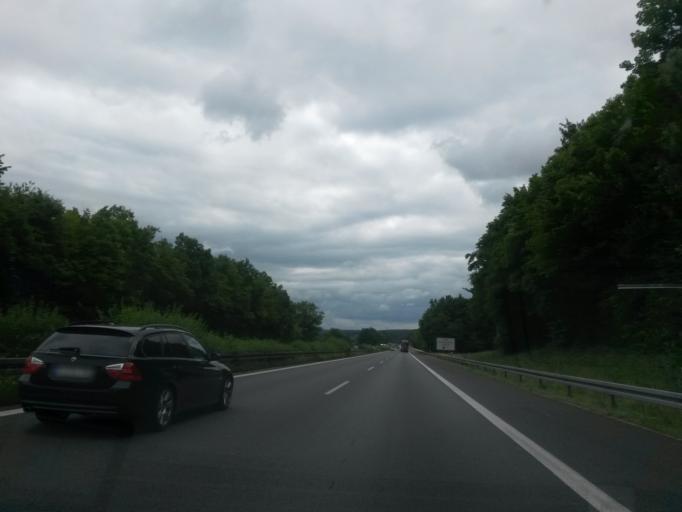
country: DE
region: Bavaria
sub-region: Upper Franconia
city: Schlusselfeld
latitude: 49.7547
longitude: 10.6103
